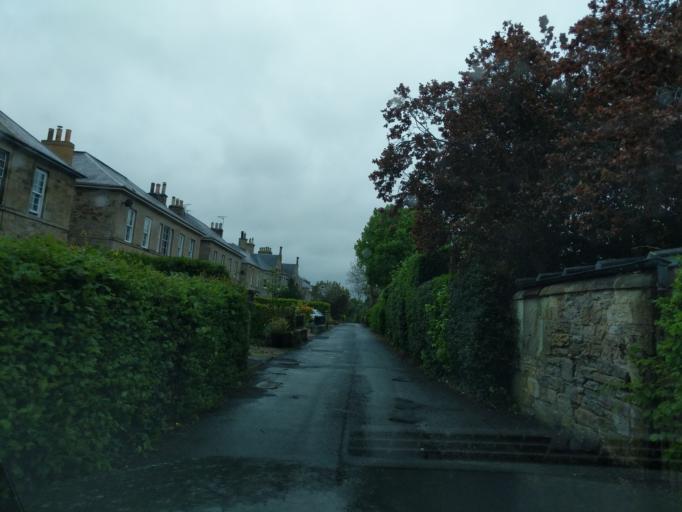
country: GB
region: Scotland
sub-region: The Scottish Borders
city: Kelso
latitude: 55.6023
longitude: -2.4339
